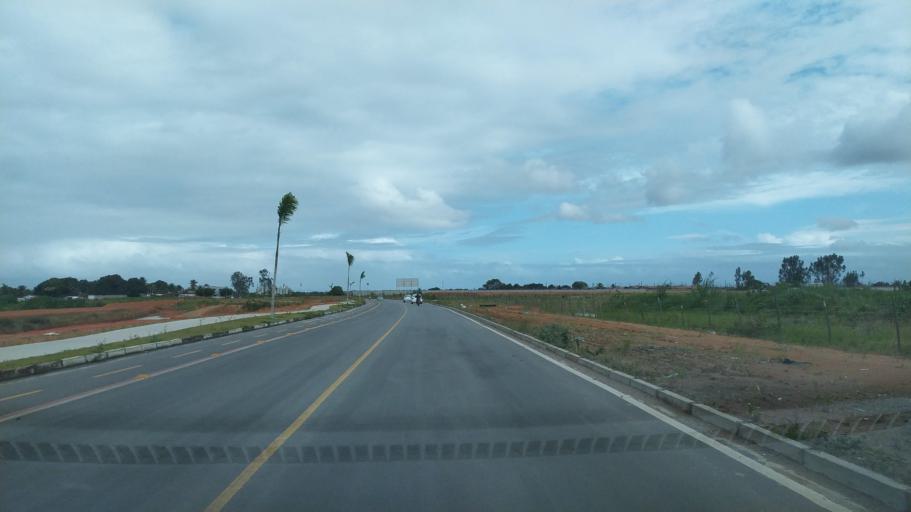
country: BR
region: Alagoas
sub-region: Satuba
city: Satuba
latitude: -9.5373
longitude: -35.7664
